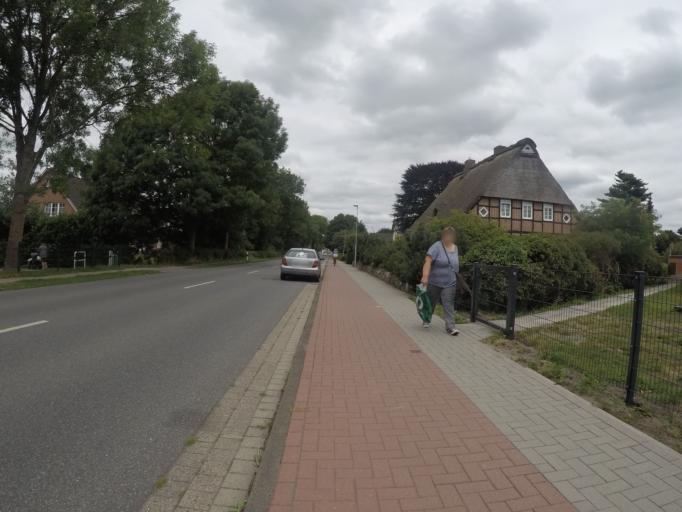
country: DE
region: Lower Saxony
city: Himmelpforten
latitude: 53.6194
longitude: 9.3068
